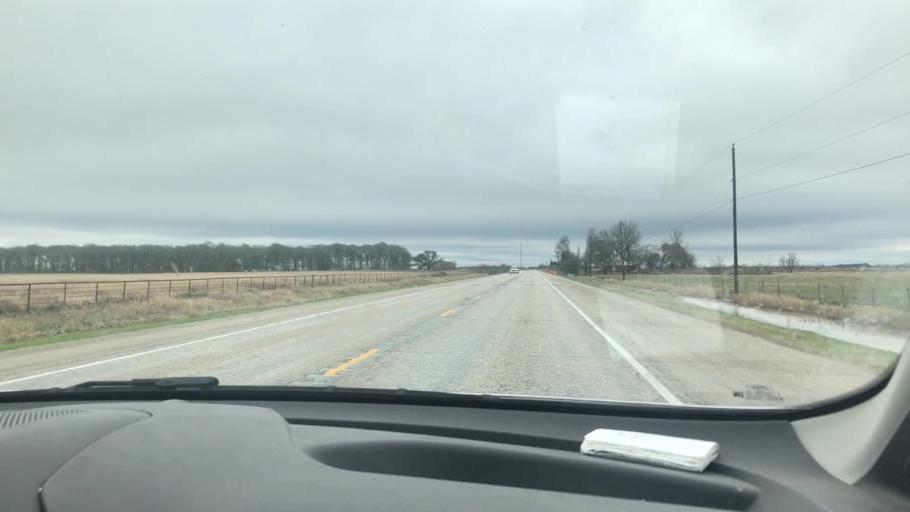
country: US
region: Texas
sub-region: Wharton County
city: Wharton
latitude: 29.2481
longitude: -96.0466
